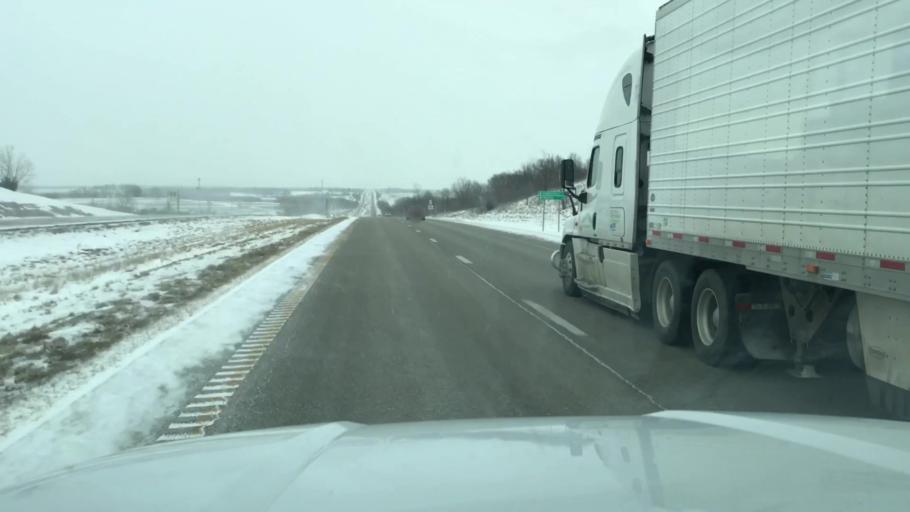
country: US
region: Missouri
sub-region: Andrew County
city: Country Club Village
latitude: 39.7475
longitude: -94.6855
